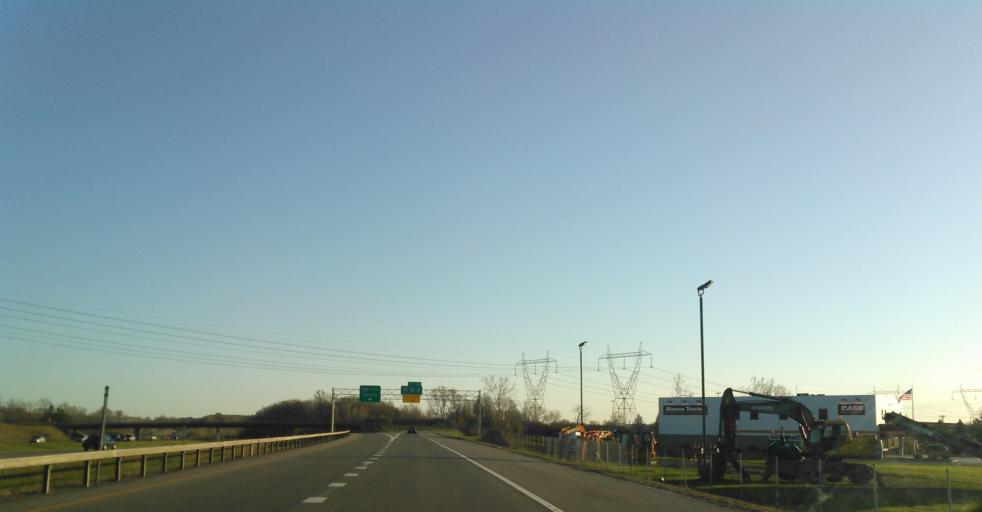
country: US
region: New York
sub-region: Monroe County
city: Rochester
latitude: 43.0559
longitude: -77.6450
